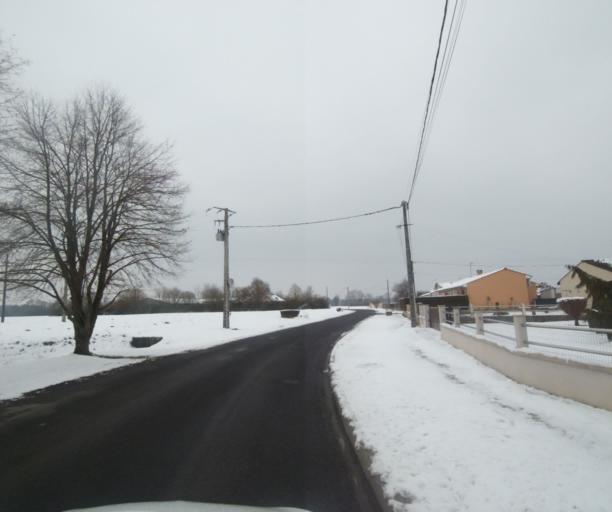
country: FR
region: Champagne-Ardenne
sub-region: Departement de la Haute-Marne
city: Saint-Dizier
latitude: 48.5801
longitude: 4.8968
